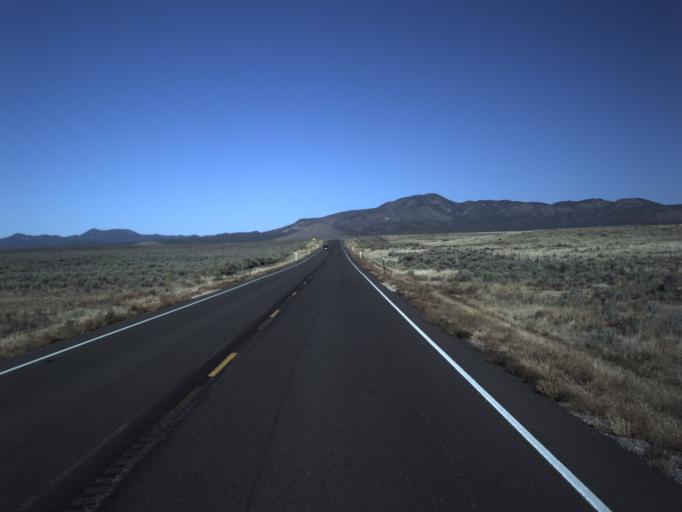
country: US
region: Utah
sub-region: Washington County
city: Enterprise
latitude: 37.7839
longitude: -113.8682
